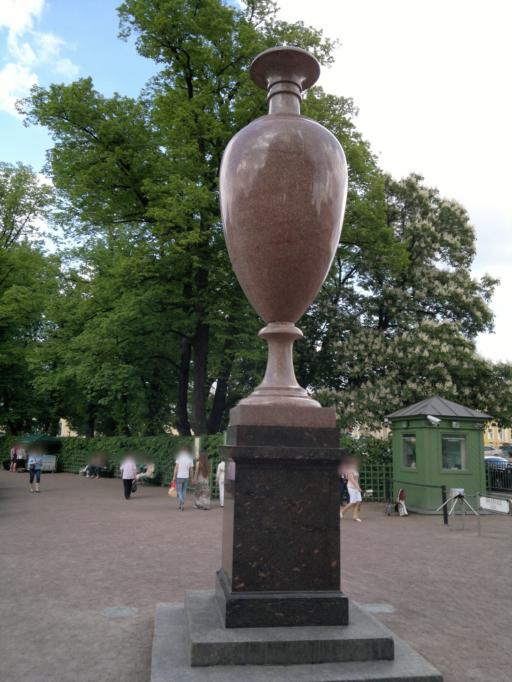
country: RU
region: St.-Petersburg
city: Saint Petersburg
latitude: 59.9419
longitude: 30.3366
